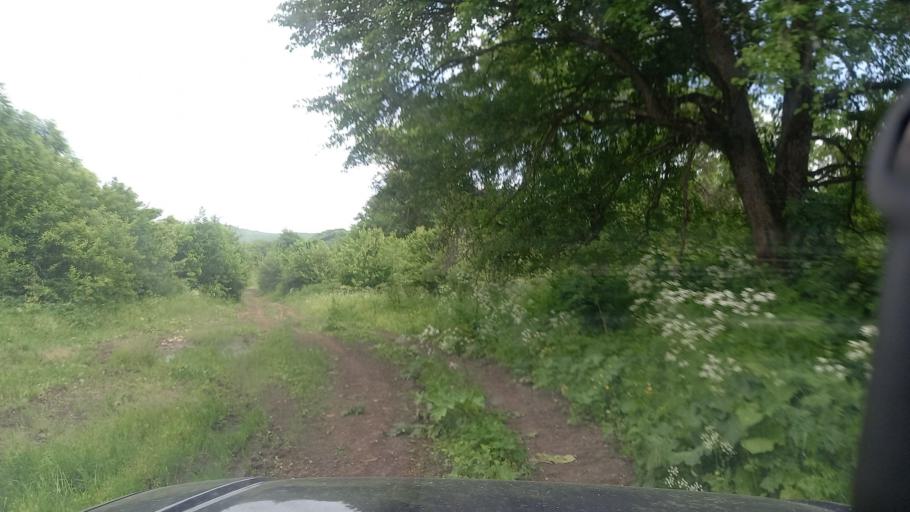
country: RU
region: Karachayevo-Cherkesiya
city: Pregradnaya
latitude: 44.0776
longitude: 41.2568
